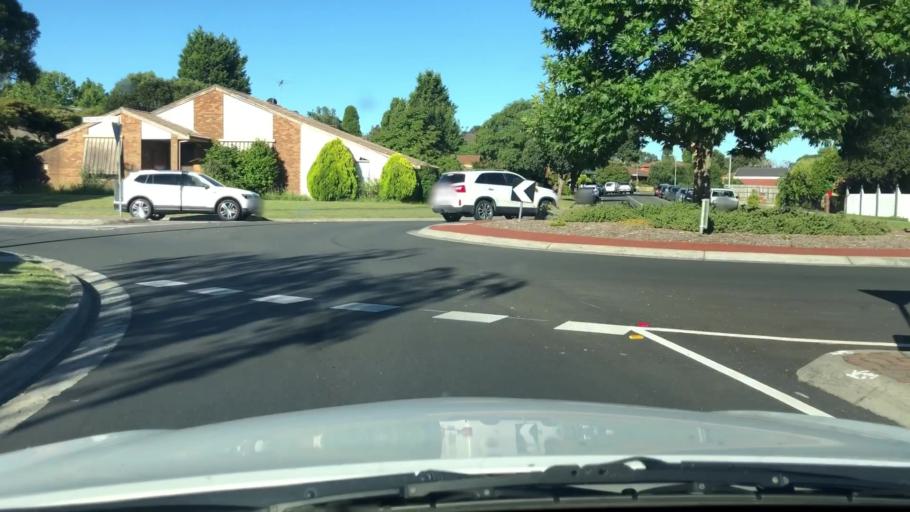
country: AU
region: Victoria
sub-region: Knox
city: Rowville
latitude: -37.9290
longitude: 145.2412
